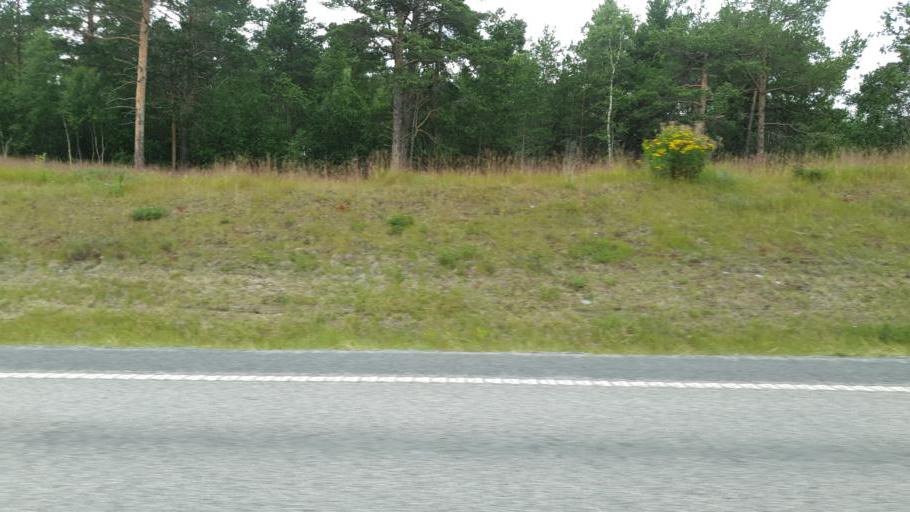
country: NO
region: Sor-Trondelag
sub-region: Oppdal
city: Oppdal
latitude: 62.5803
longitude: 9.6671
